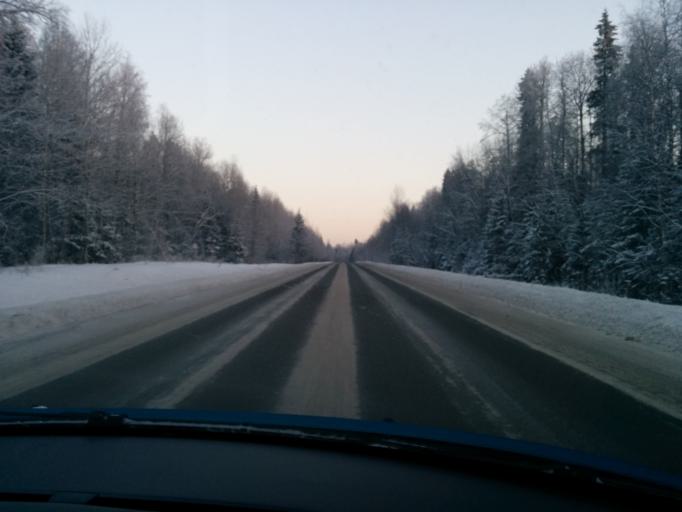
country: RU
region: Perm
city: Novyye Lyady
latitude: 58.0283
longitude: 56.5008
